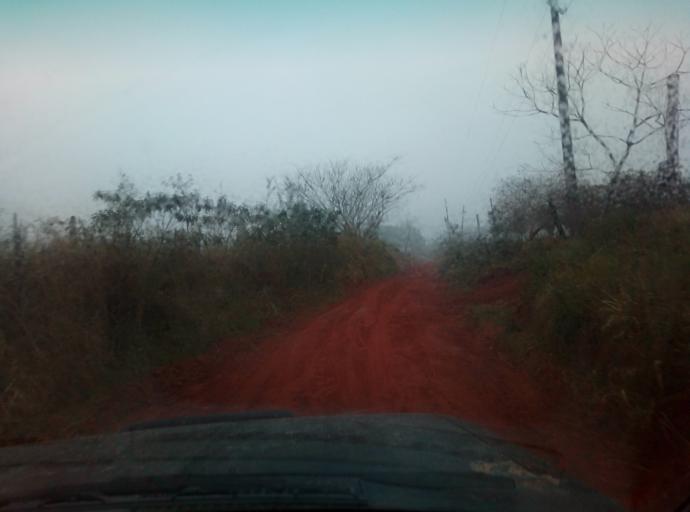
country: PY
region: Caaguazu
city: Doctor Cecilio Baez
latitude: -25.1607
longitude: -56.2619
